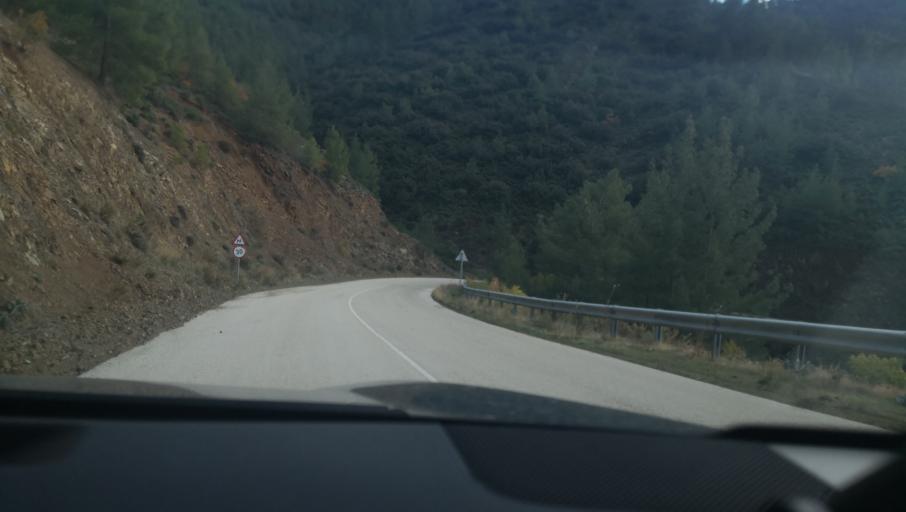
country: CY
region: Lefkosia
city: Lefka
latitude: 35.0540
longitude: 32.7480
